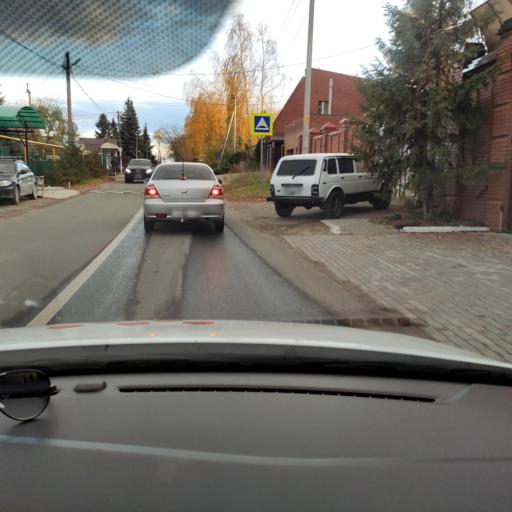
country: RU
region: Tatarstan
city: Verkhniy Uslon
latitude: 55.6223
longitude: 49.0138
